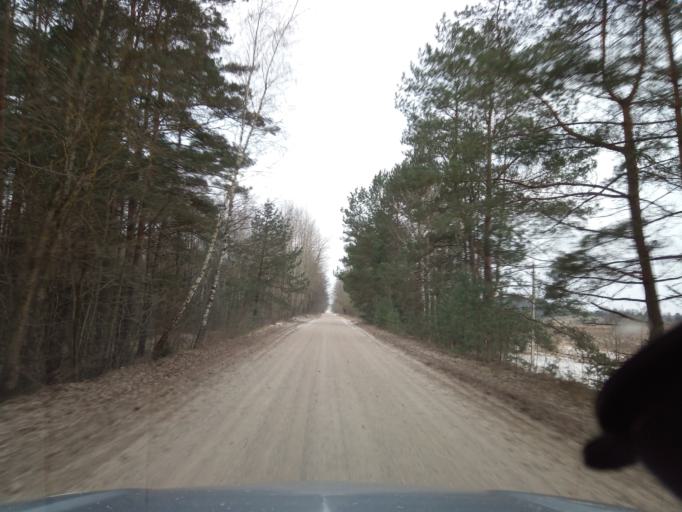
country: LT
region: Alytaus apskritis
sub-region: Alytaus rajonas
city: Daugai
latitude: 54.3183
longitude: 24.3368
